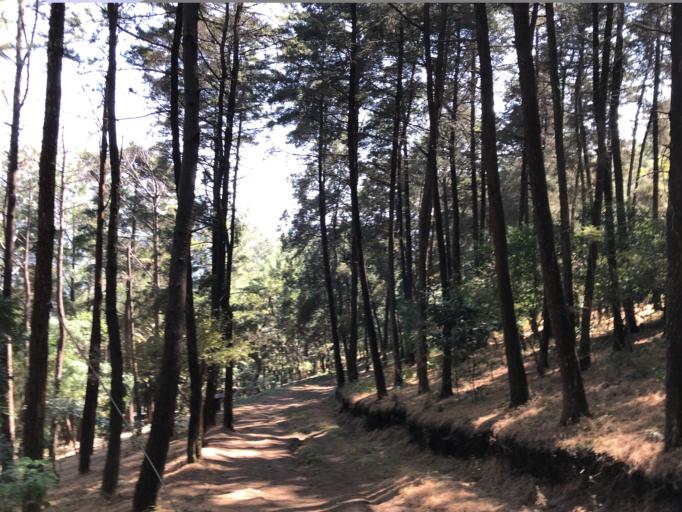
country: GT
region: Guatemala
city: Villa Canales
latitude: 14.4816
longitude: -90.5476
